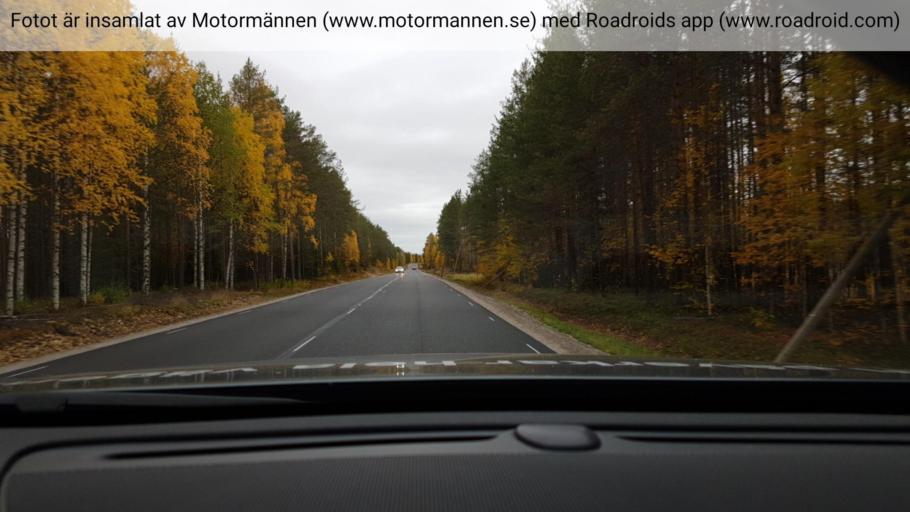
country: SE
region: Norrbotten
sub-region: Overkalix Kommun
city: OEverkalix
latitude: 66.4357
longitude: 22.7931
